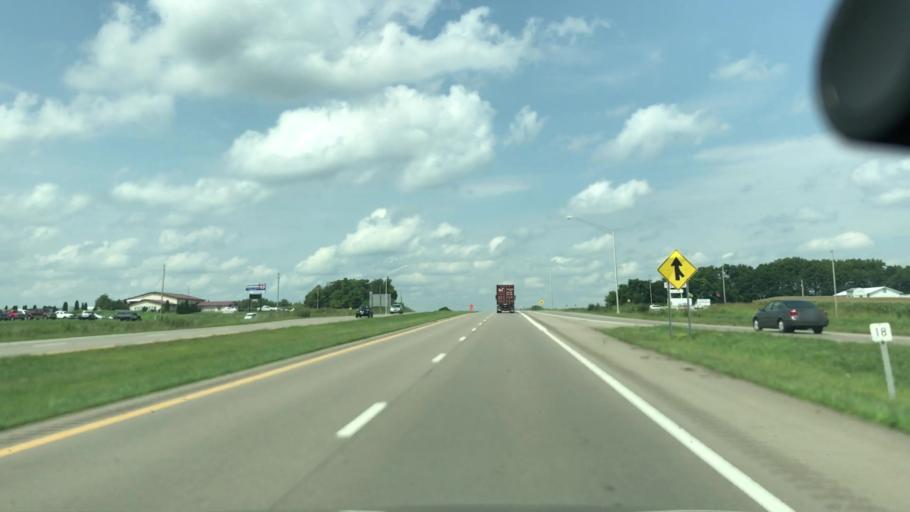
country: US
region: Ohio
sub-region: Ross County
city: Kingston
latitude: 39.4183
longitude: -82.9751
